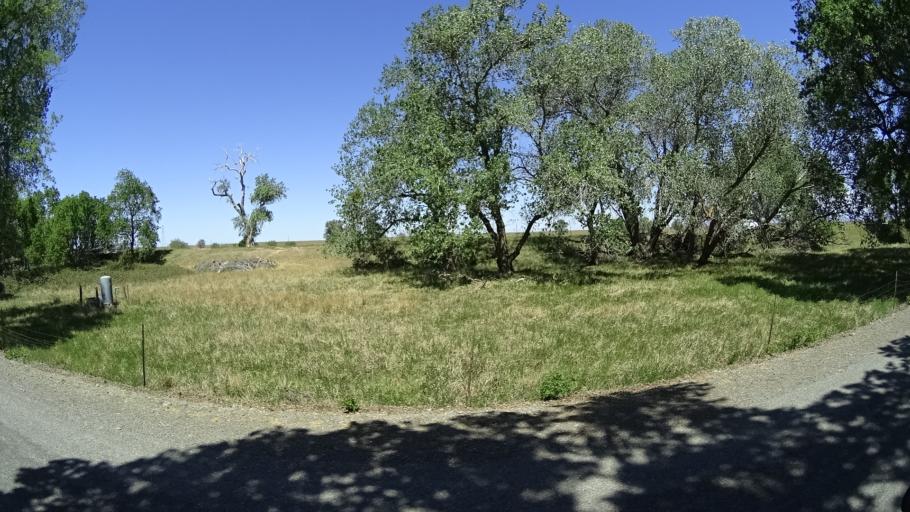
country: US
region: California
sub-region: Glenn County
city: Orland
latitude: 39.7951
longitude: -122.2433
